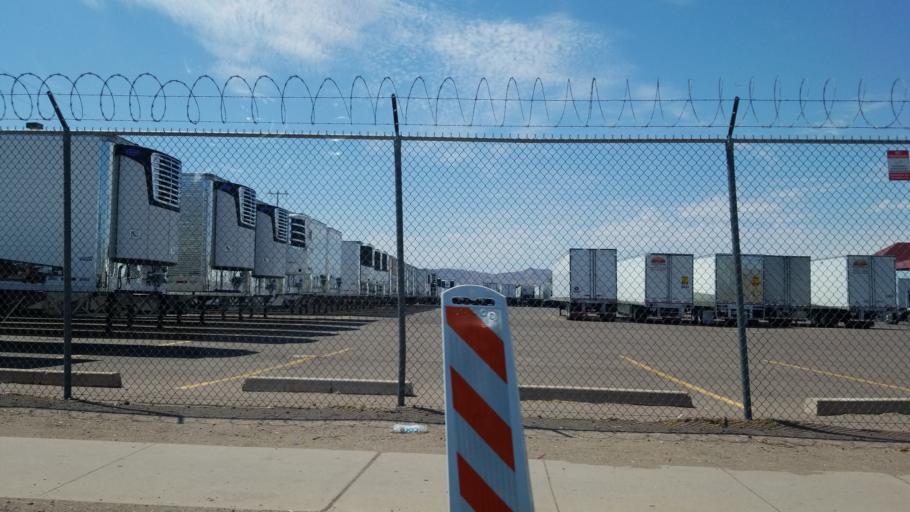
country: US
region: Arizona
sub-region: Maricopa County
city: Phoenix
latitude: 33.4367
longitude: -112.1187
